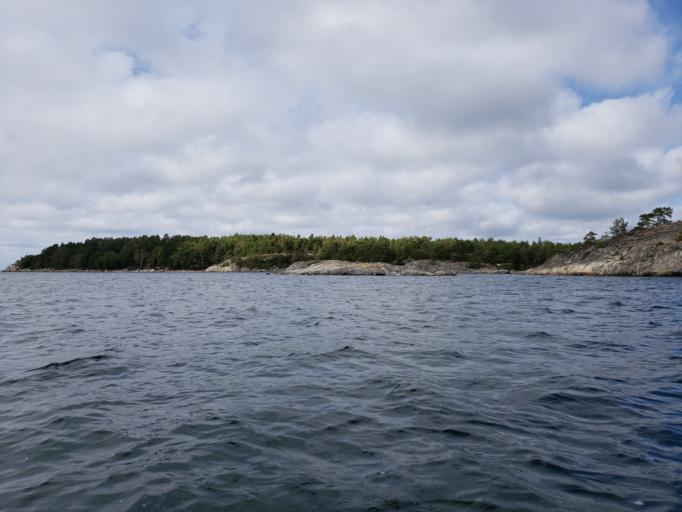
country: FI
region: Varsinais-Suomi
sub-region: Aboland-Turunmaa
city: Dragsfjaerd
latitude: 59.9032
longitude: 22.3561
